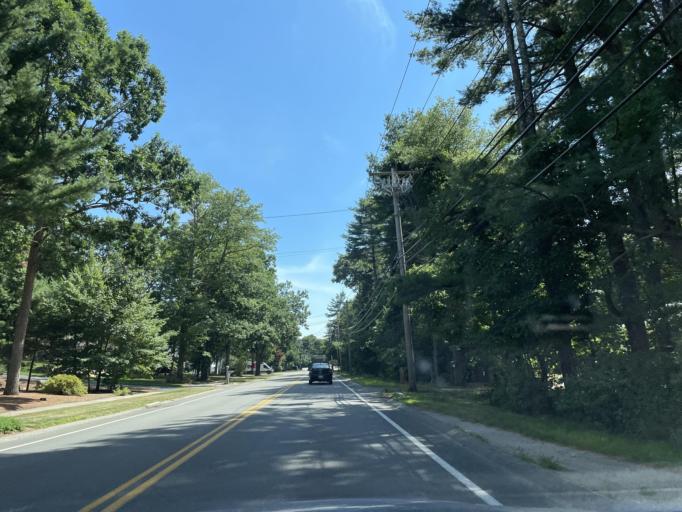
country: US
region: Massachusetts
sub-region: Norfolk County
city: Foxborough
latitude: 42.0807
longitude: -71.2323
